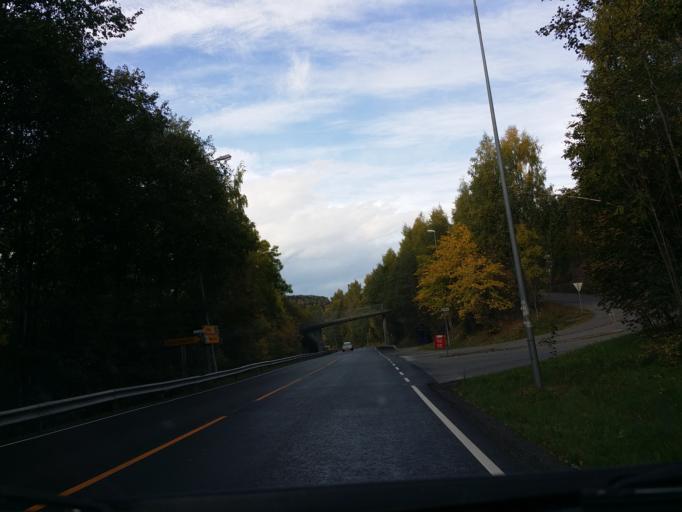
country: NO
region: Akershus
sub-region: Baerum
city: Sandvika
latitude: 59.9244
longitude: 10.4978
